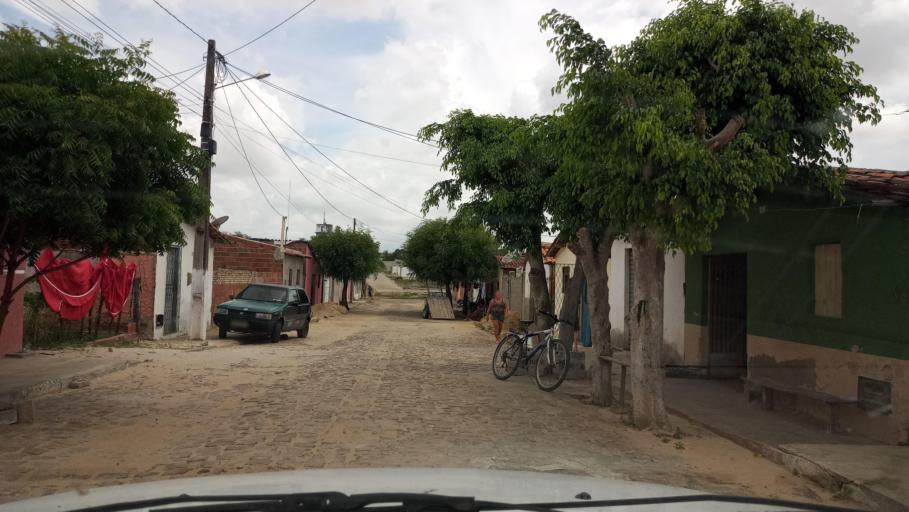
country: BR
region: Rio Grande do Norte
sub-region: Tangara
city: Tangara
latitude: -6.1100
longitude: -35.7147
